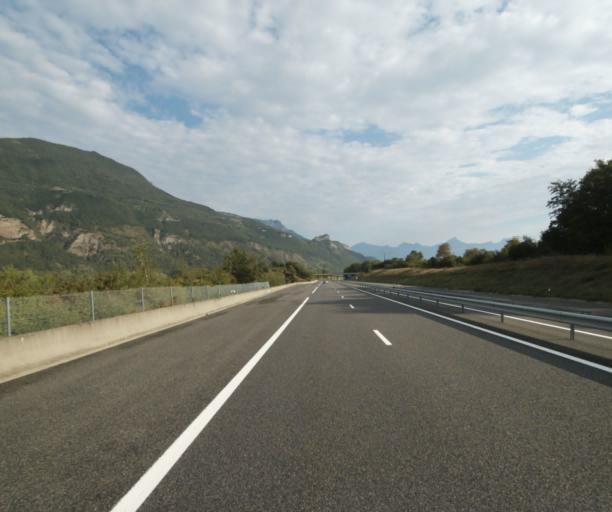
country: FR
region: Rhone-Alpes
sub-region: Departement de l'Isere
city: Vif
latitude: 45.0287
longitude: 5.6624
